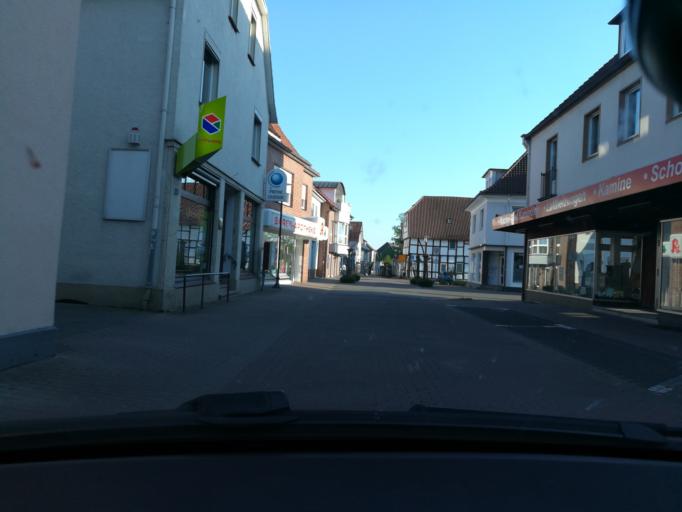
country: DE
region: North Rhine-Westphalia
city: Versmold
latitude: 52.0418
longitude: 8.1554
